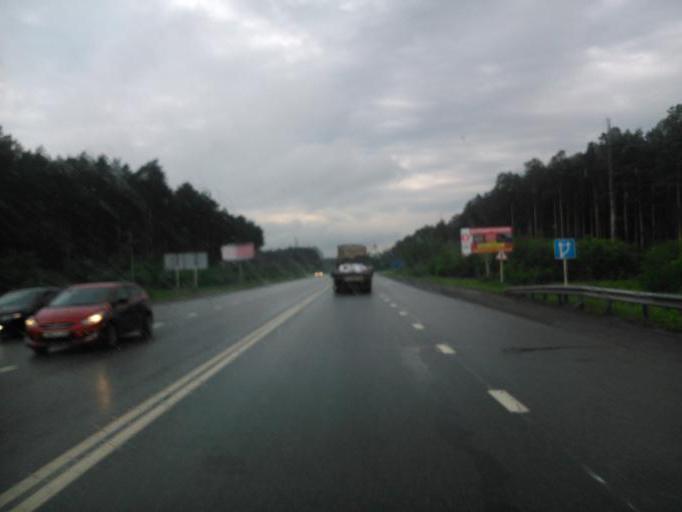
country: RU
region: Sverdlovsk
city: Beryozovsky
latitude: 56.9067
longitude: 60.7574
